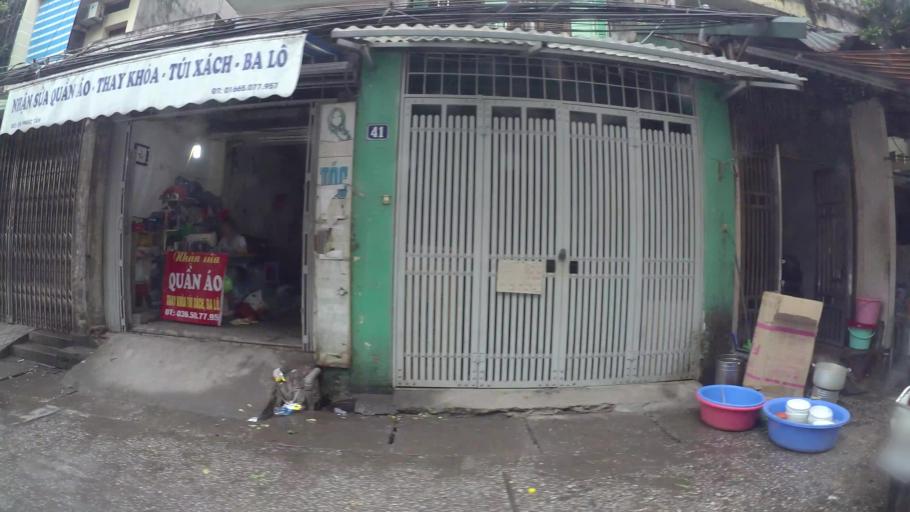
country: VN
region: Ha Noi
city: Hoan Kiem
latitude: 21.0384
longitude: 105.8537
